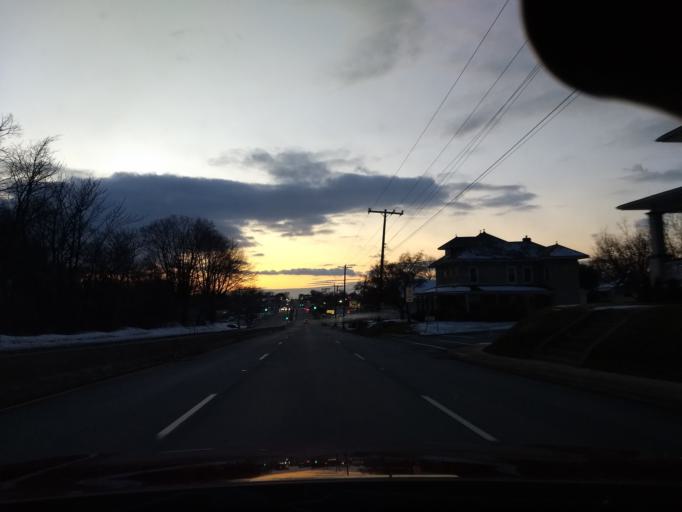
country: US
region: New Jersey
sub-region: Warren County
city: Phillipsburg
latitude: 40.6984
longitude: -75.1705
